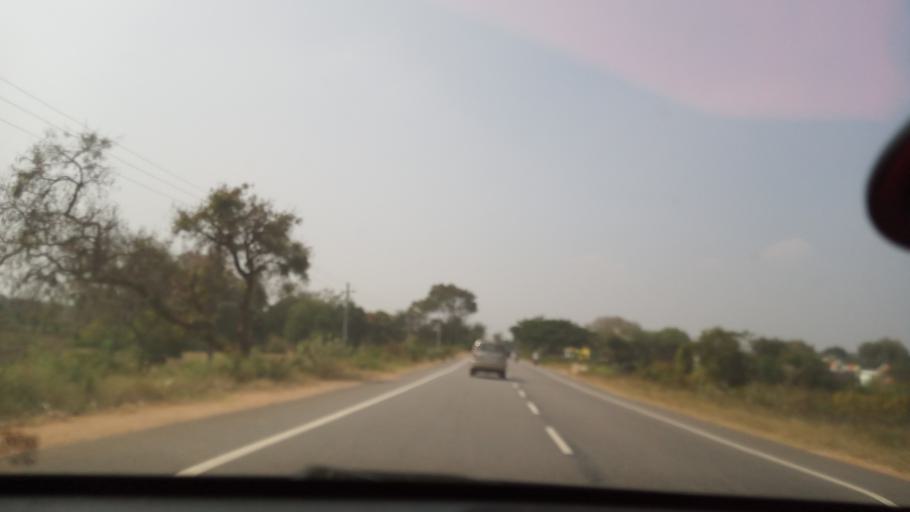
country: IN
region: Karnataka
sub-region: Mysore
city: Nanjangud
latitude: 12.0685
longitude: 76.7484
